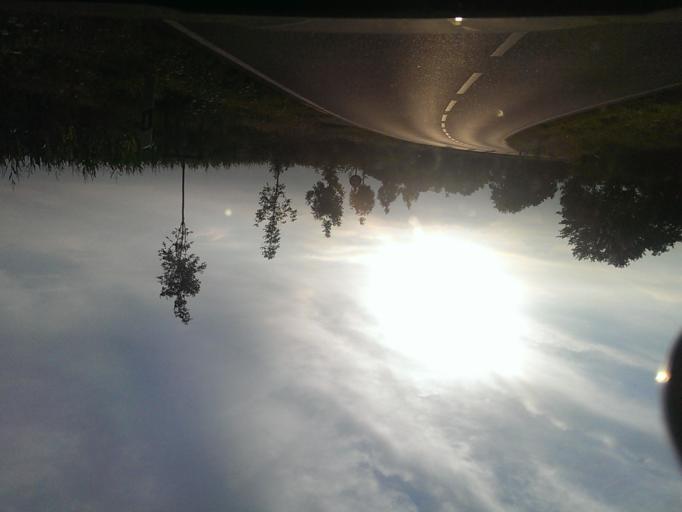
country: DE
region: Lower Saxony
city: Lilienthal
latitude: 53.1654
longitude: 8.9188
